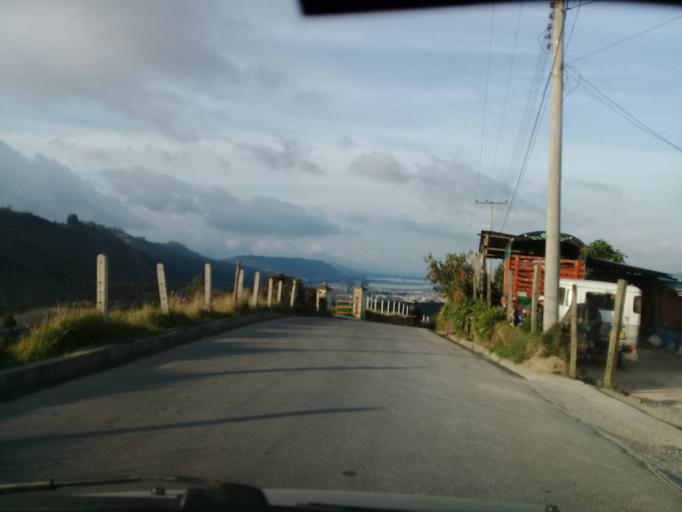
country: CO
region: Cundinamarca
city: Sibate
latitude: 4.4568
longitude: -74.2683
